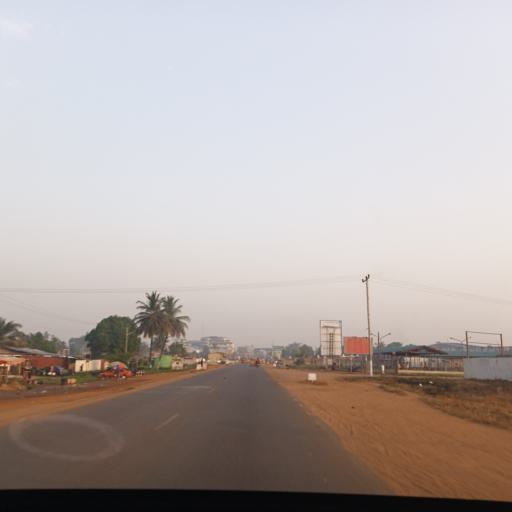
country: LR
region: Montserrado
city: Monrovia
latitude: 6.2581
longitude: -10.7041
